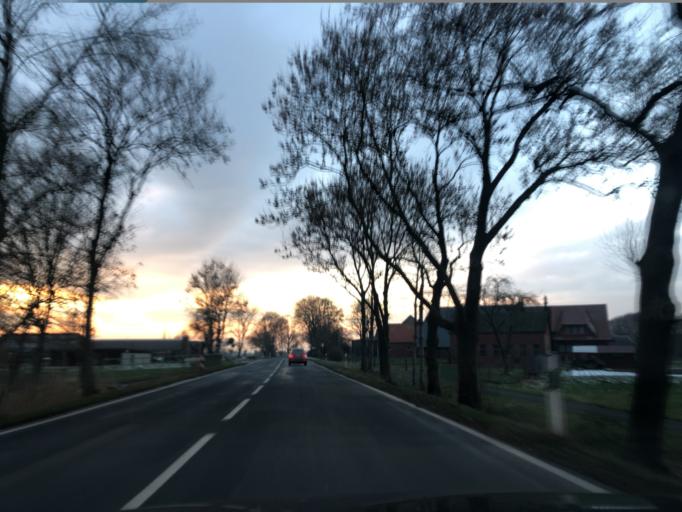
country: DE
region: Lower Saxony
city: Lemwerder
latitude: 53.1365
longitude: 8.6047
